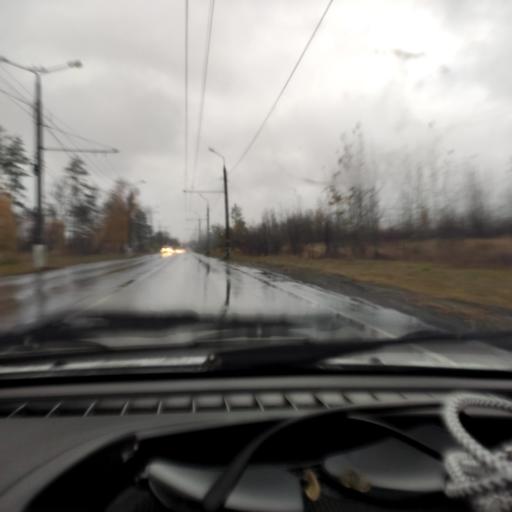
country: RU
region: Samara
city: Tol'yatti
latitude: 53.4835
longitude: 49.3795
